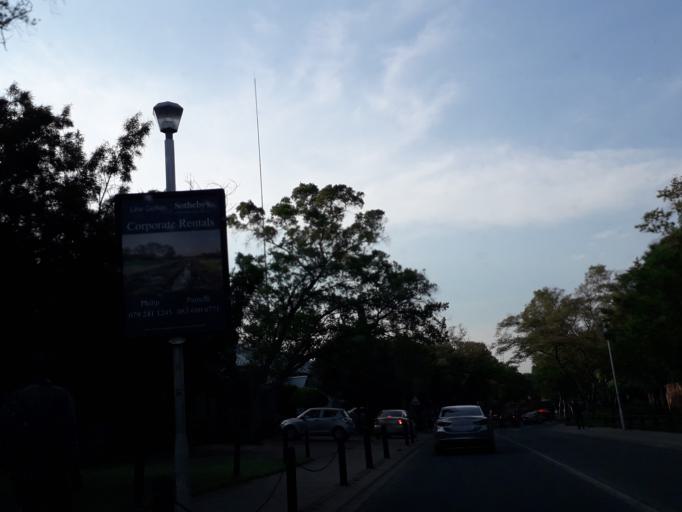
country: ZA
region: Gauteng
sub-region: City of Johannesburg Metropolitan Municipality
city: Diepsloot
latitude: -26.0069
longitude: 28.0028
